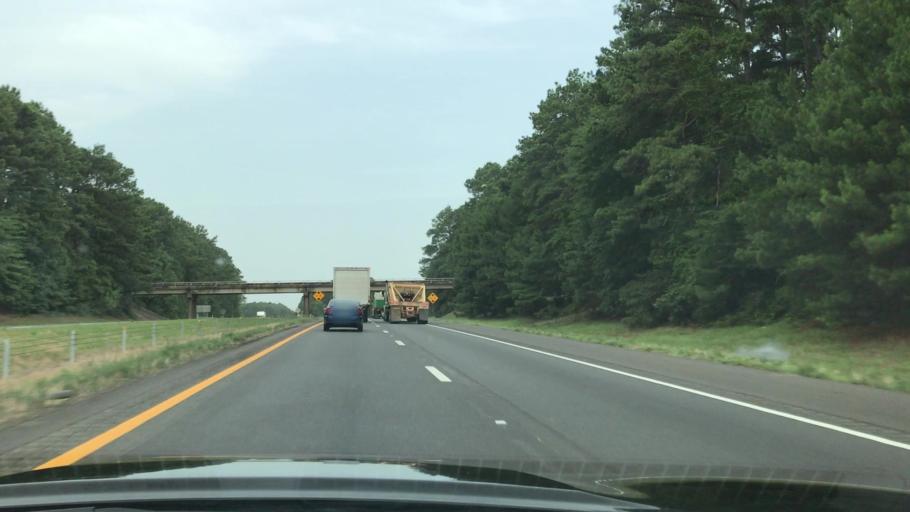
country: US
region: Texas
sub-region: Harrison County
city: Marshall
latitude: 32.4883
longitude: -94.4281
